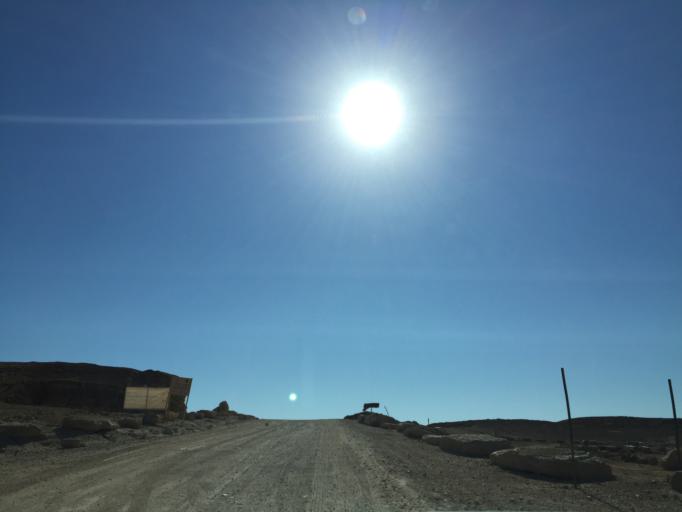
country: IL
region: Southern District
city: Mitzpe Ramon
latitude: 30.6200
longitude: 34.9204
